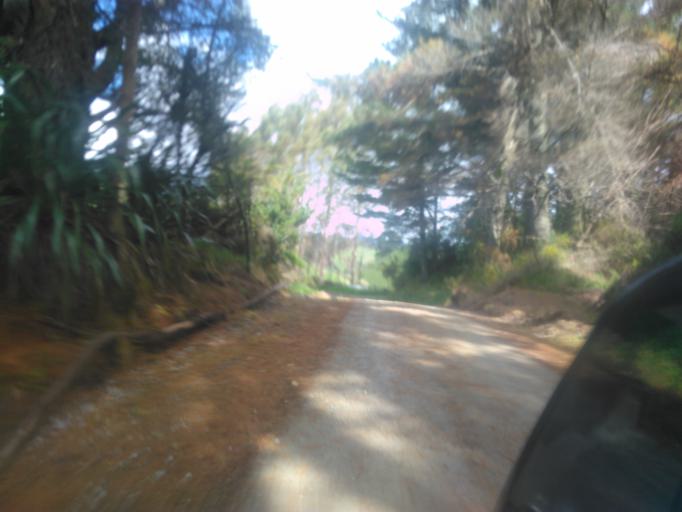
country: NZ
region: Hawke's Bay
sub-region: Wairoa District
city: Wairoa
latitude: -38.7780
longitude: 177.6131
